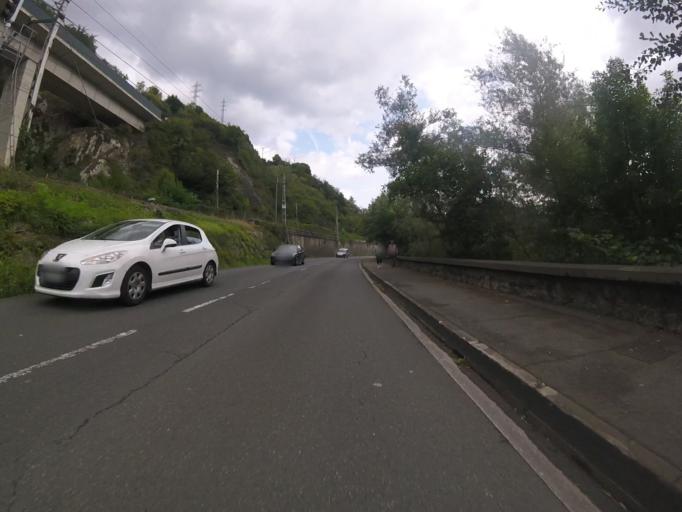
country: ES
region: Basque Country
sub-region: Provincia de Guipuzcoa
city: Tolosa
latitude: 43.1299
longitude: -2.0873
